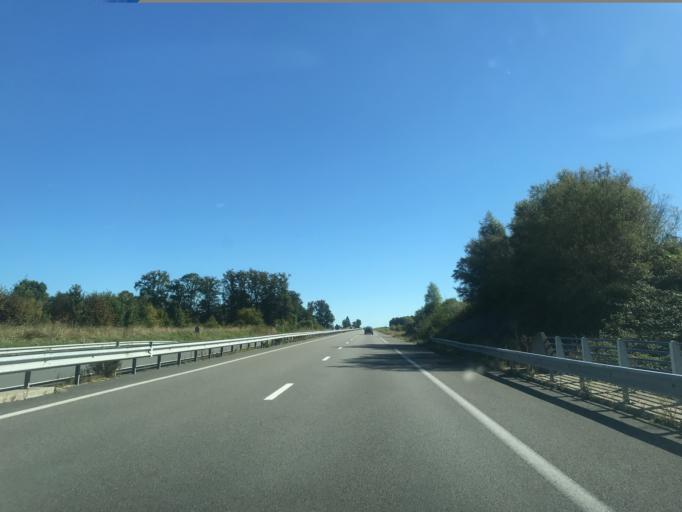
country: FR
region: Limousin
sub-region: Departement de la Creuse
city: Gouzon
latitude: 46.2304
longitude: 2.3106
